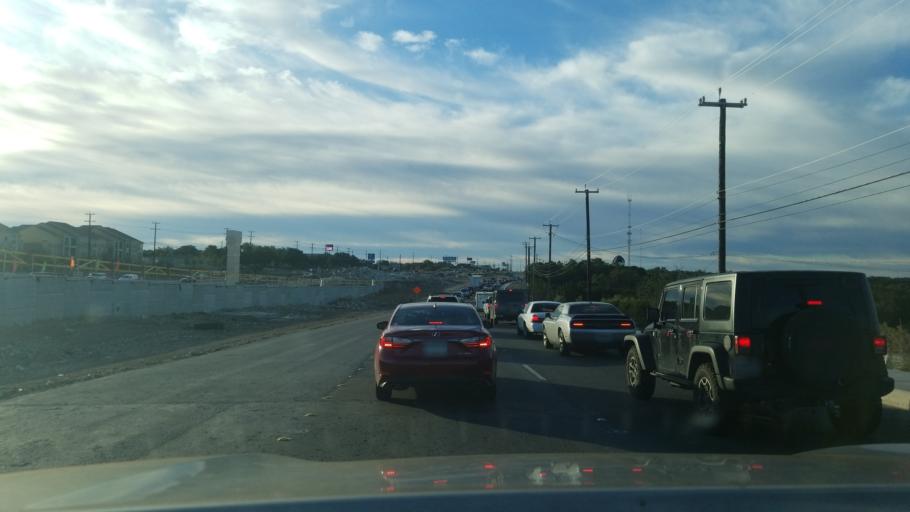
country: US
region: Texas
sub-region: Bexar County
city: Timberwood Park
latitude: 29.6701
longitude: -98.4512
